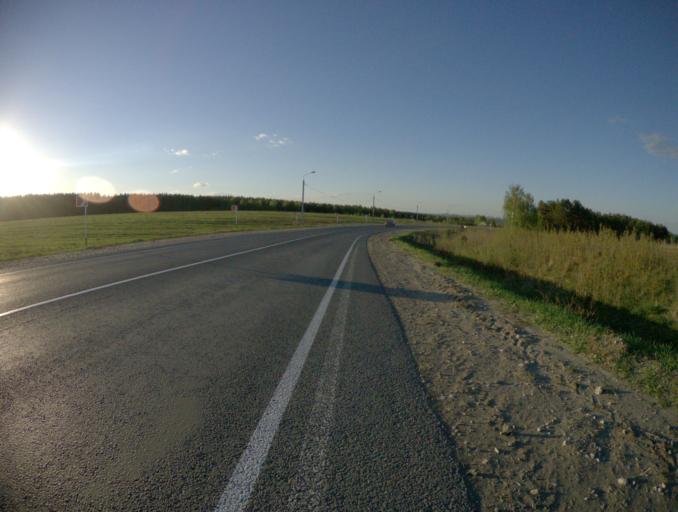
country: RU
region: Vladimir
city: Raduzhnyy
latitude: 56.0093
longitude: 40.3062
